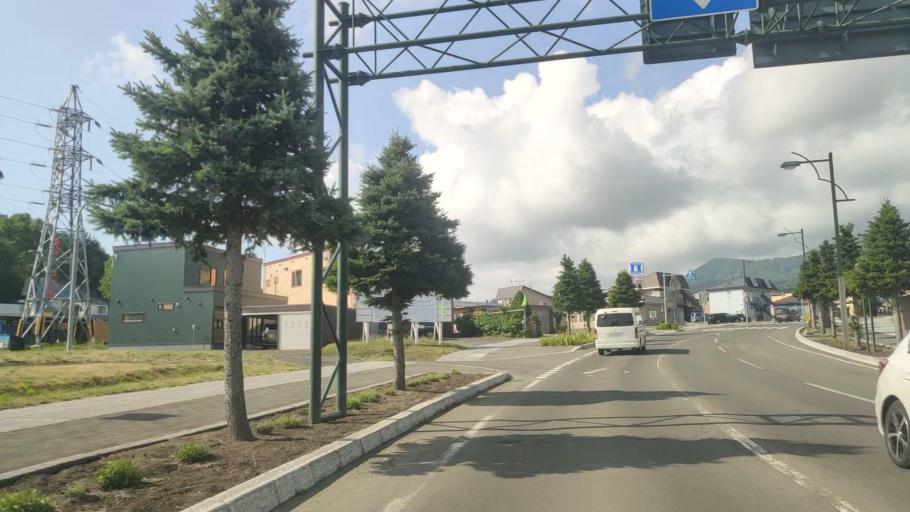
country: JP
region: Hokkaido
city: Shimo-furano
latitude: 43.3446
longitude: 142.3709
